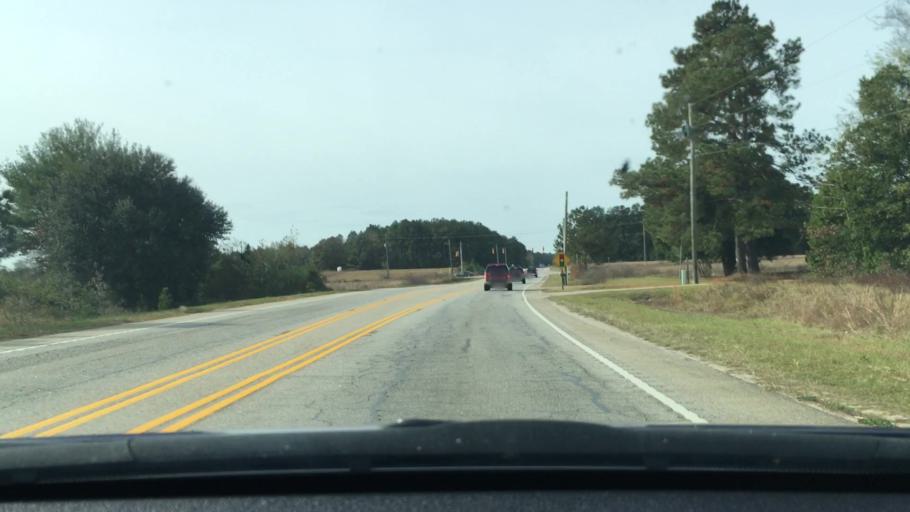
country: US
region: South Carolina
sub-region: Sumter County
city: Cherryvale
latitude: 33.9379
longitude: -80.4725
